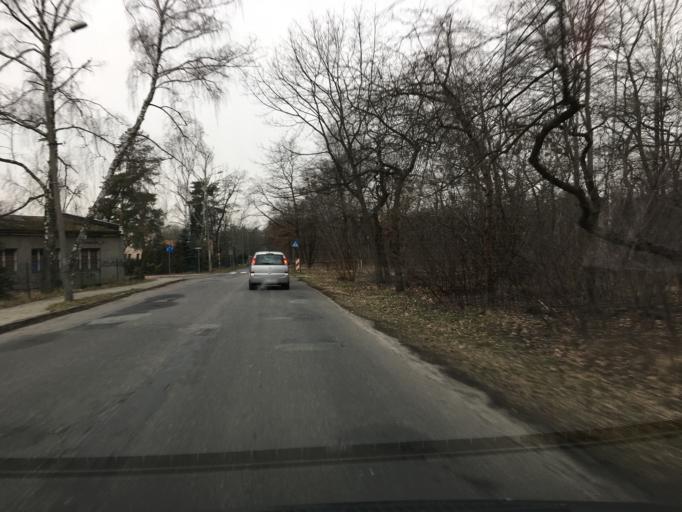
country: PL
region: Opole Voivodeship
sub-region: Powiat kedzierzynsko-kozielski
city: Kedzierzyn-Kozle
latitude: 50.3196
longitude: 18.2435
